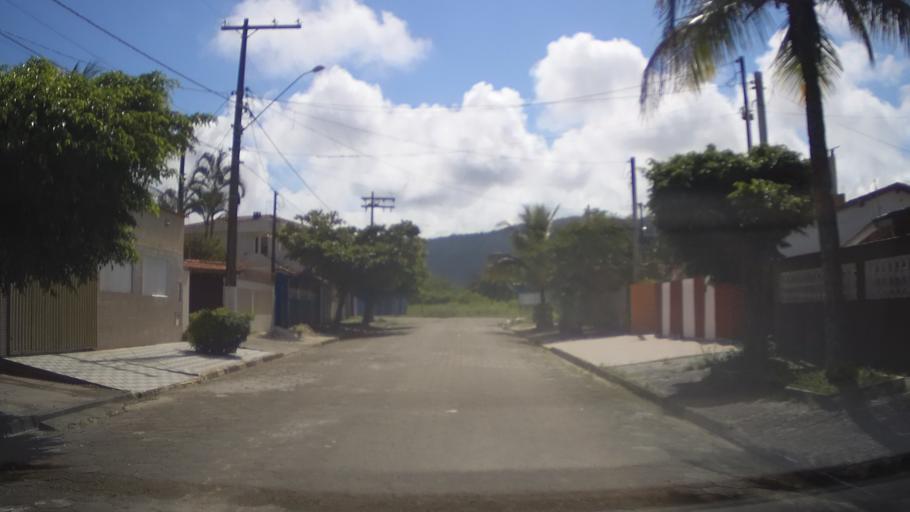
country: BR
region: Sao Paulo
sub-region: Itanhaem
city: Itanhaem
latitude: -24.1497
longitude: -46.7247
